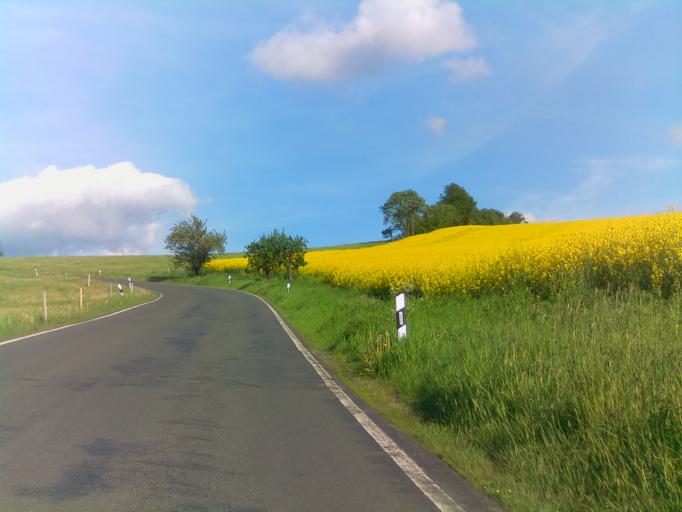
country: DE
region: Thuringia
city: Mellenbach-Glasbach
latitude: 50.6305
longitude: 11.0936
